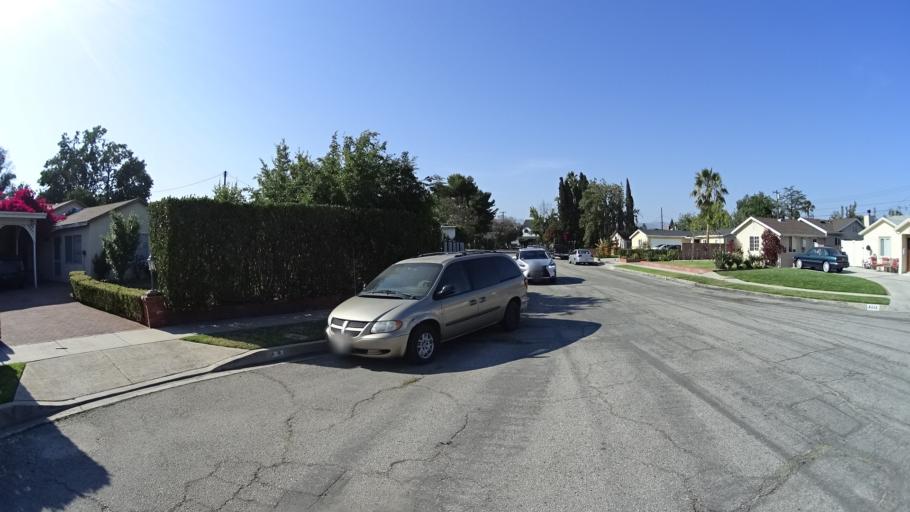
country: US
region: California
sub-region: Los Angeles County
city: Van Nuys
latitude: 34.2162
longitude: -118.4218
